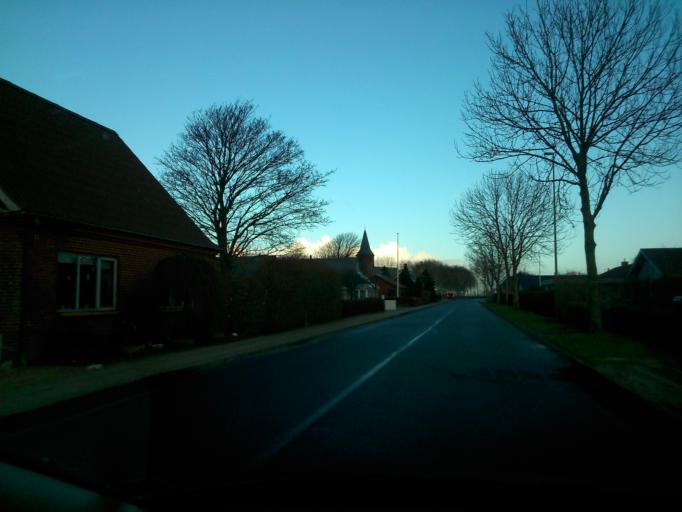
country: DK
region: Central Jutland
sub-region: Ringkobing-Skjern Kommune
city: Videbaek
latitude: 56.0678
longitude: 8.6052
